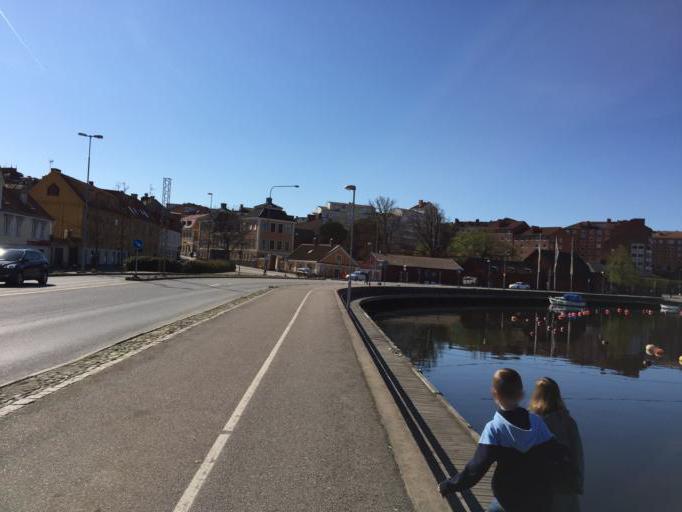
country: SE
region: Blekinge
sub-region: Karlskrona Kommun
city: Karlskrona
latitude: 56.1635
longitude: 15.5810
